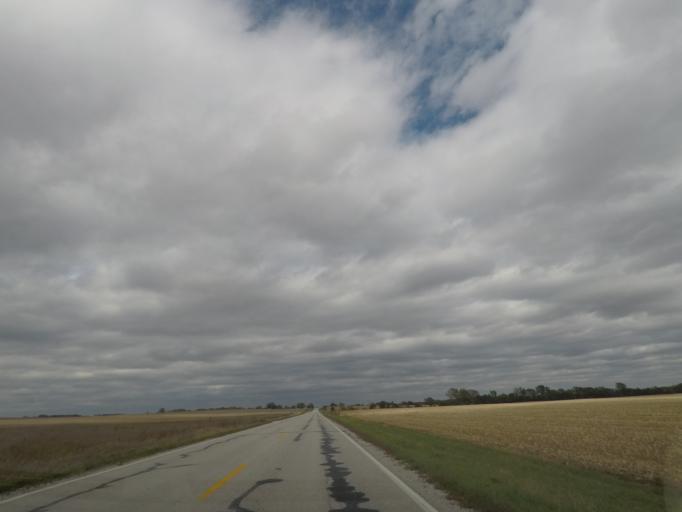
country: US
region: Iowa
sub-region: Story County
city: Huxley
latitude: 41.8525
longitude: -93.5316
